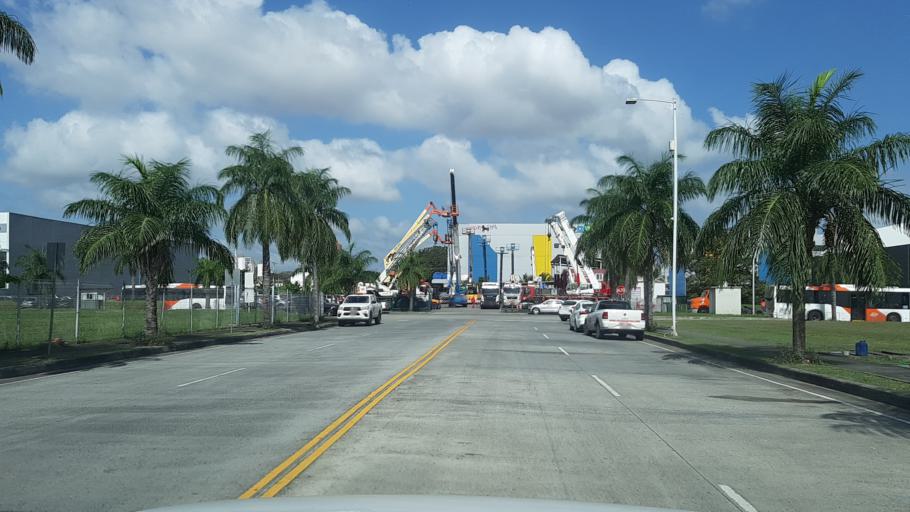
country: PA
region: Panama
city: San Miguelito
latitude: 9.0315
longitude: -79.4583
